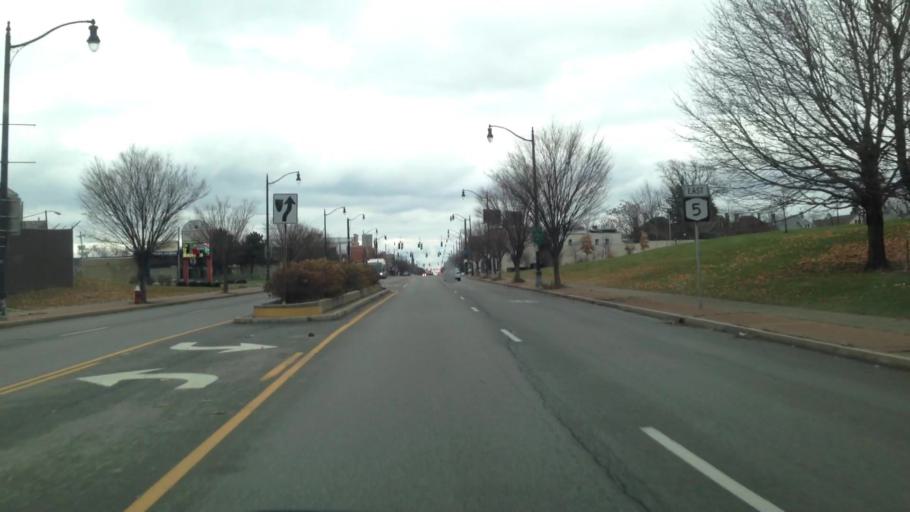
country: US
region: New York
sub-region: Erie County
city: Eggertsville
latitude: 42.9462
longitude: -78.8314
